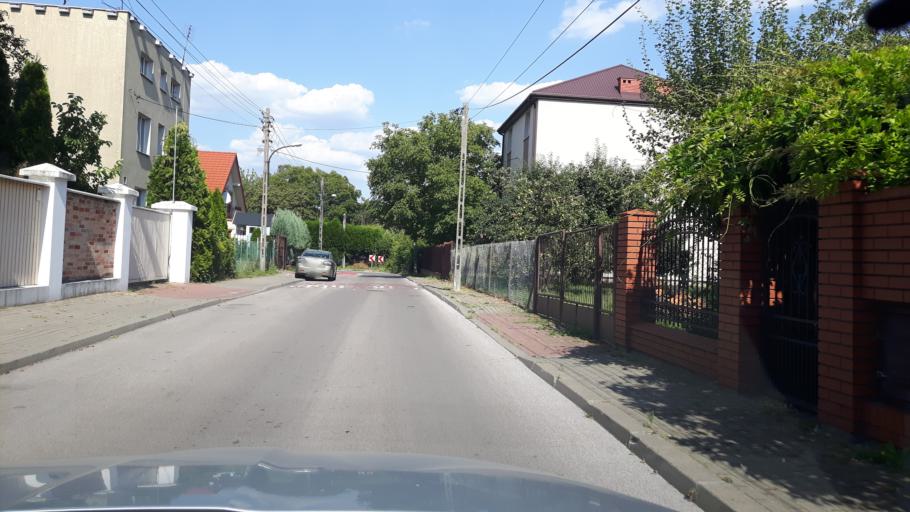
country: PL
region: Masovian Voivodeship
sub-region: Warszawa
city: Wlochy
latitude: 52.2097
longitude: 20.9325
